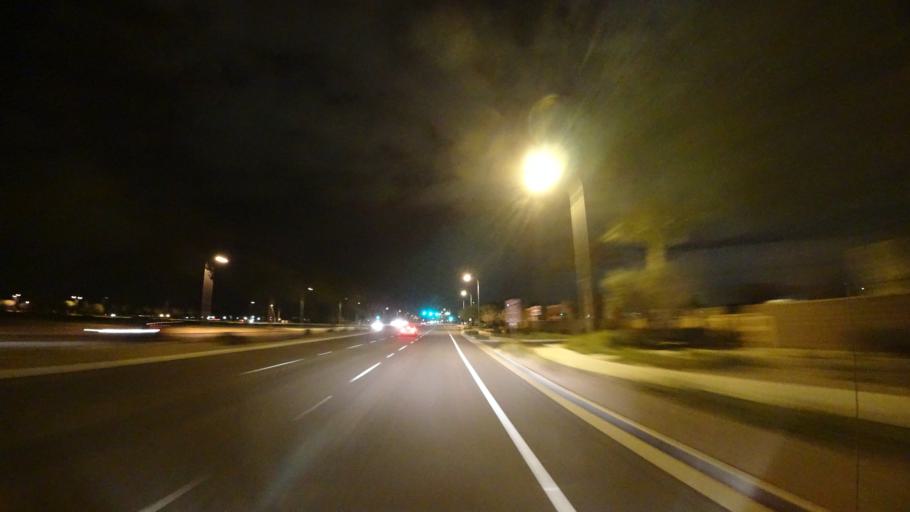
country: US
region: Arizona
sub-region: Maricopa County
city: Chandler
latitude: 33.2917
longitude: -111.8569
